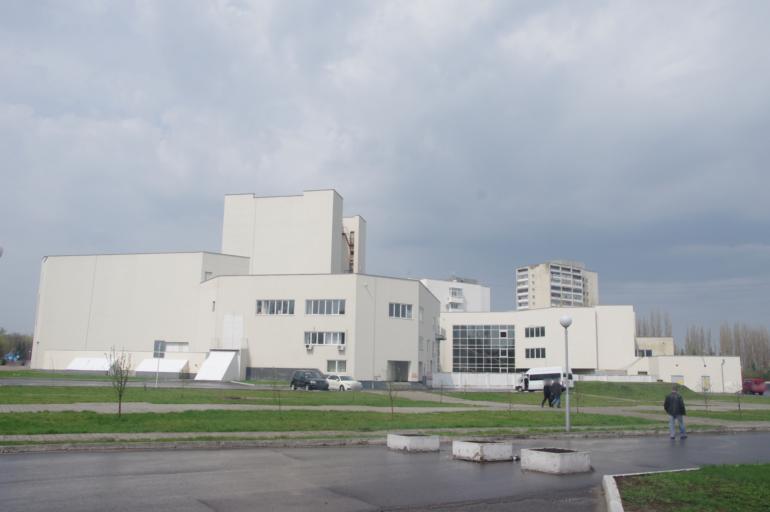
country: RU
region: Kursk
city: Kurchatov
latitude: 51.6585
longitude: 35.6611
